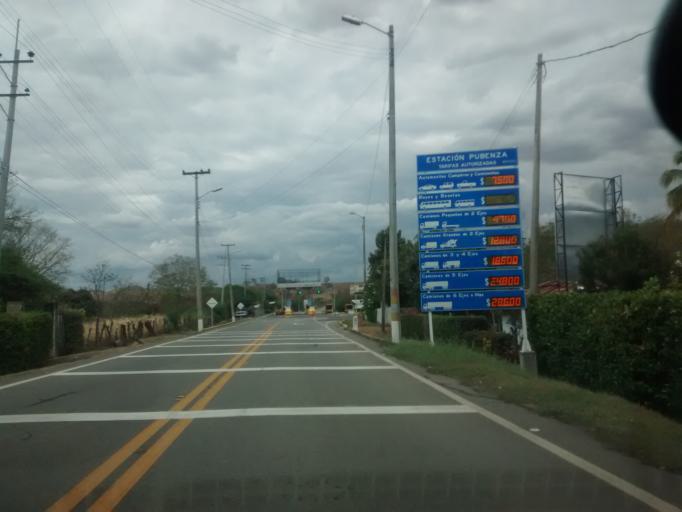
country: CO
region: Cundinamarca
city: Agua de Dios
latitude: 4.4023
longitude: -74.7327
